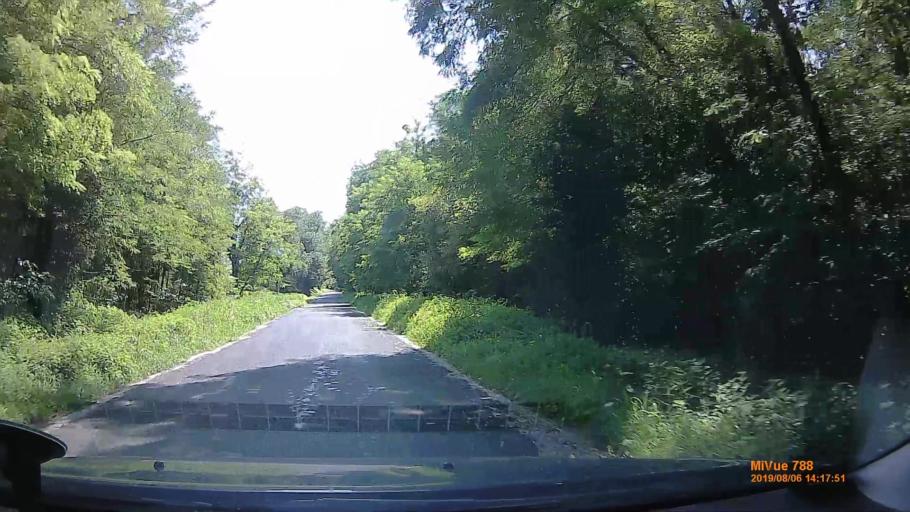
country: HU
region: Zala
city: Zalakomar
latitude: 46.5405
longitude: 17.0826
